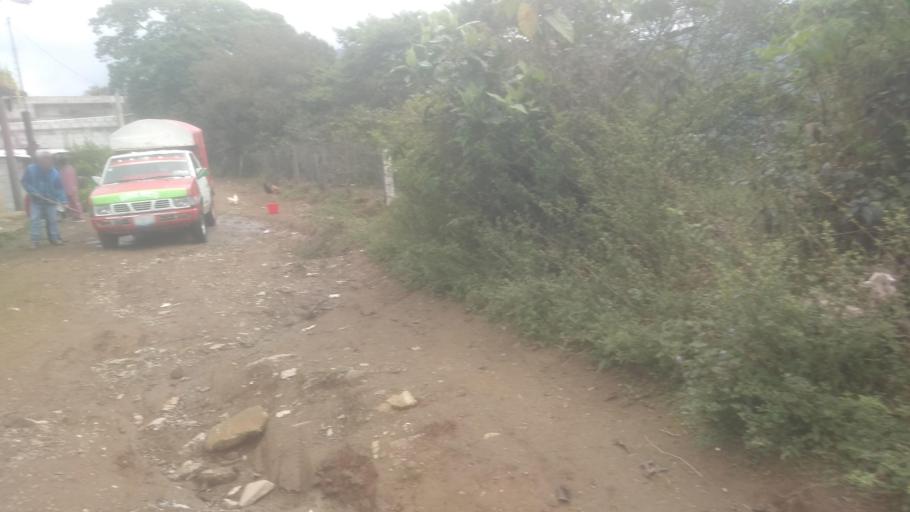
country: MX
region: Veracruz
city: Chocaman
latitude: 18.9913
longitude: -97.0540
